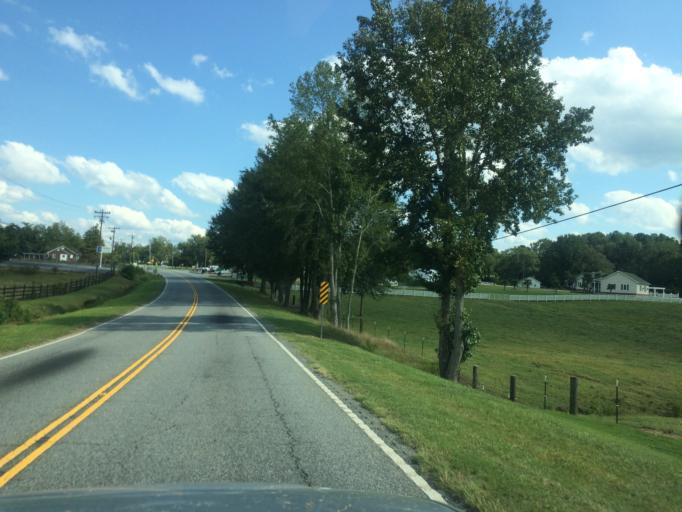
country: US
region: South Carolina
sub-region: Anderson County
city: Honea Path
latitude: 34.4558
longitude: -82.4104
